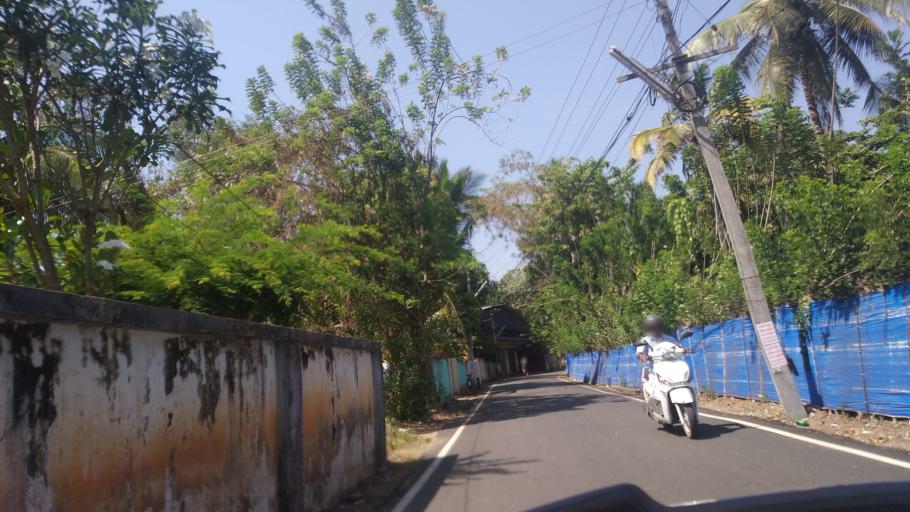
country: IN
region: Kerala
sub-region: Ernakulam
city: Elur
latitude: 10.1350
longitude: 76.2254
